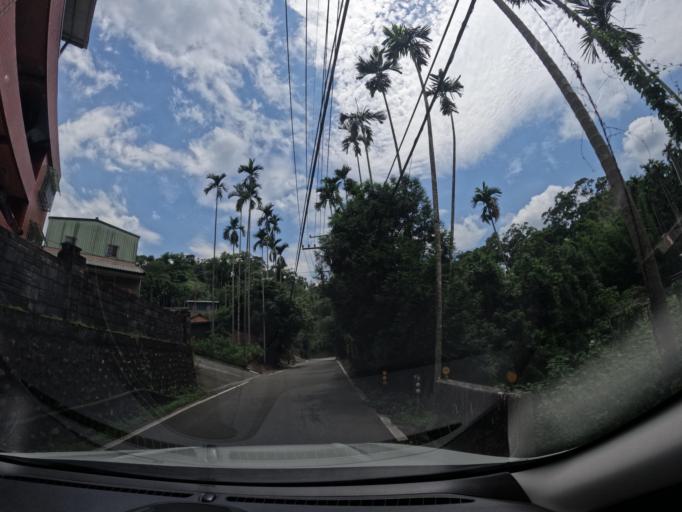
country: TW
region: Taipei
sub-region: Taipei
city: Banqiao
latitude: 24.9168
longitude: 121.4139
